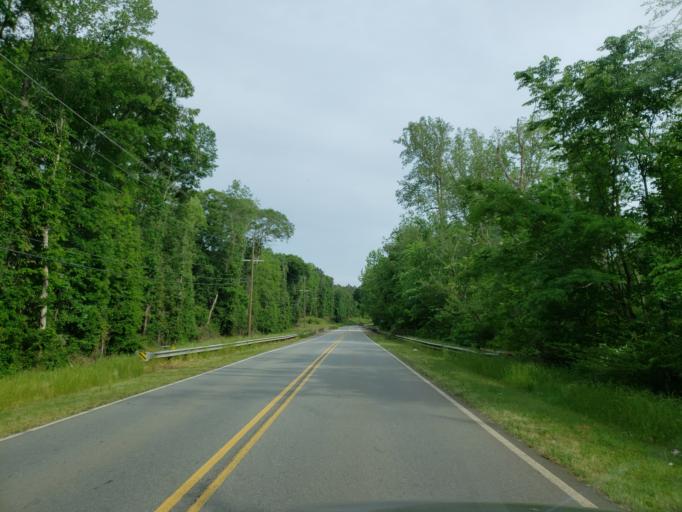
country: US
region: Georgia
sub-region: Dooly County
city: Vienna
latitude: 32.1964
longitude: -83.9032
